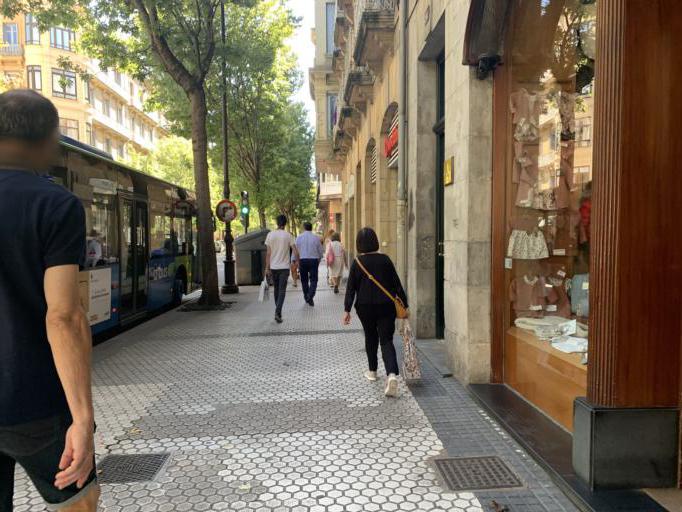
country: ES
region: Basque Country
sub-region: Provincia de Guipuzcoa
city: San Sebastian
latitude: 43.3169
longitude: -1.9826
